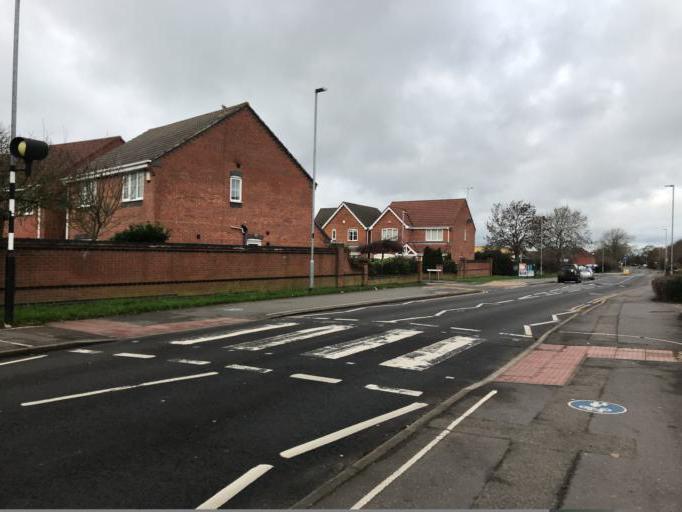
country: GB
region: England
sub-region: Leicestershire
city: Hinckley
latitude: 52.5512
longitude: -1.3832
